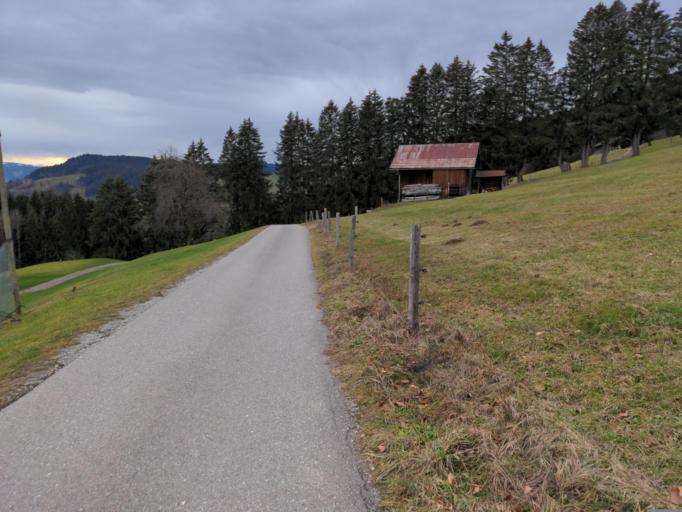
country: DE
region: Bavaria
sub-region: Swabia
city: Oberstaufen
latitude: 47.5704
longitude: 10.0404
